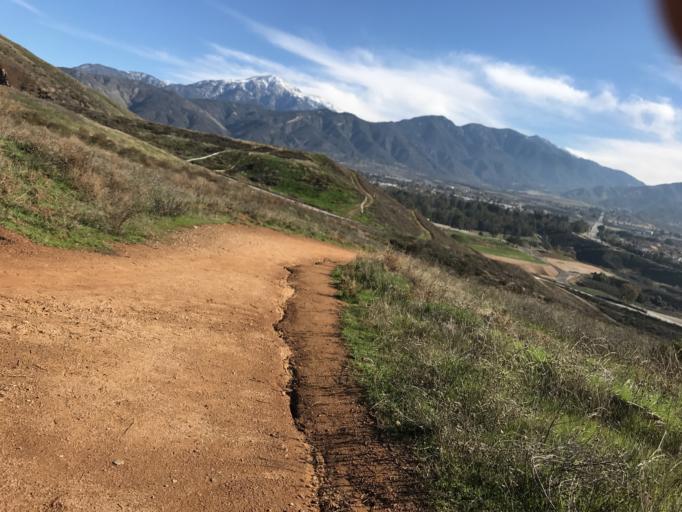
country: US
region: California
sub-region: San Bernardino County
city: Yucaipa
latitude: 34.0482
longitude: -117.0606
